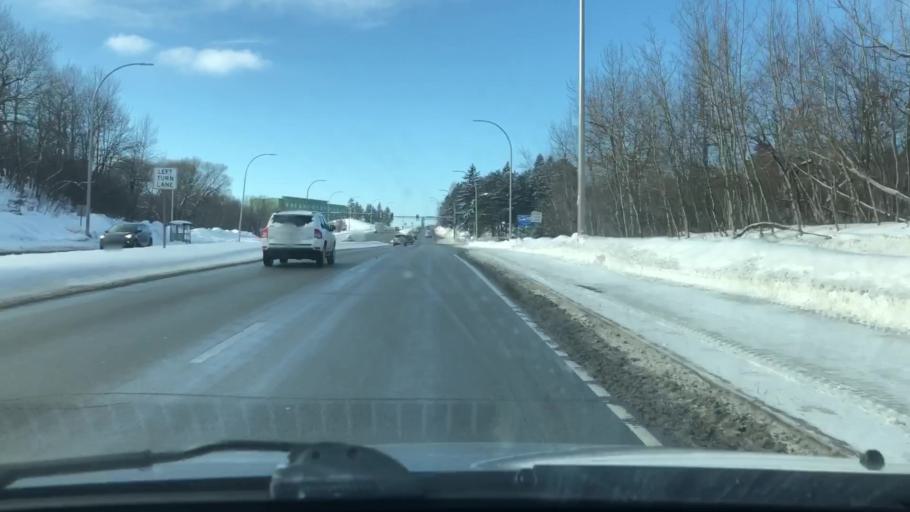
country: US
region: Minnesota
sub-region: Saint Louis County
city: Duluth
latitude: 46.7993
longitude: -92.1141
